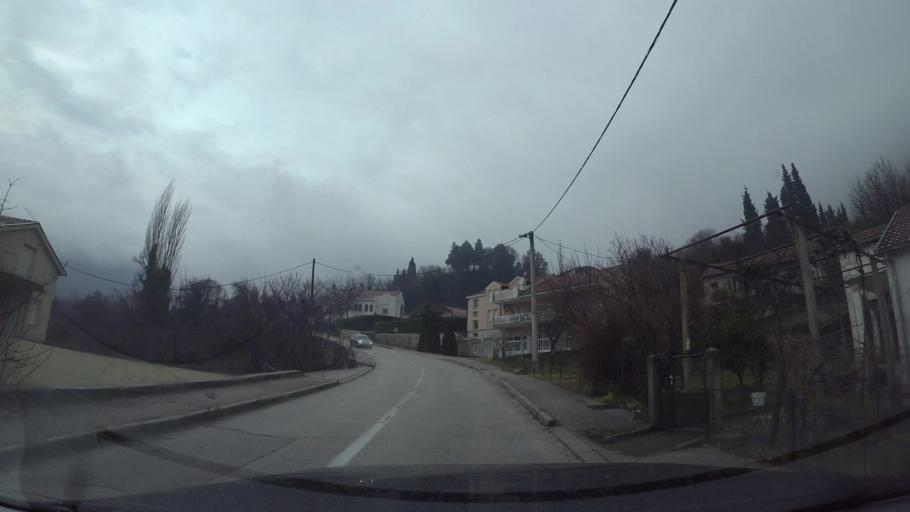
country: BA
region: Federation of Bosnia and Herzegovina
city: Cim
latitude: 43.3564
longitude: 17.7735
